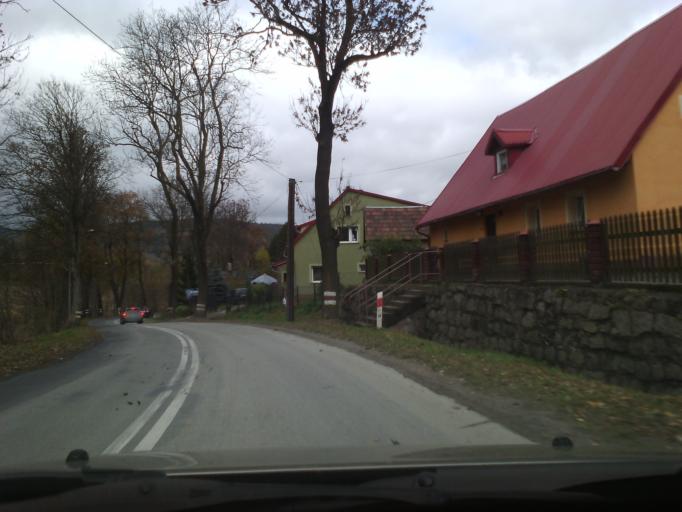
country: PL
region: Lower Silesian Voivodeship
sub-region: Powiat jeleniogorski
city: Kowary
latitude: 50.7694
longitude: 15.8996
